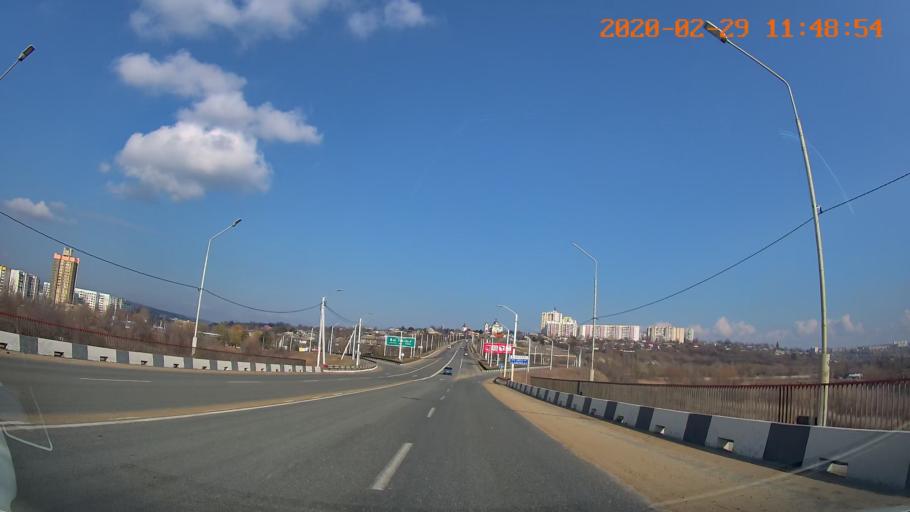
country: MD
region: Telenesti
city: Ribnita
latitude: 47.7512
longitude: 28.9929
